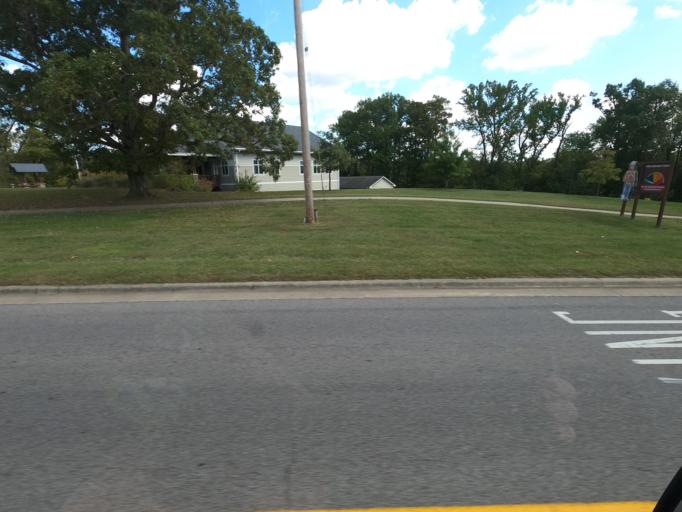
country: US
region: Illinois
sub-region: Johnson County
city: Vienna
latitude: 37.4207
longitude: -88.8932
